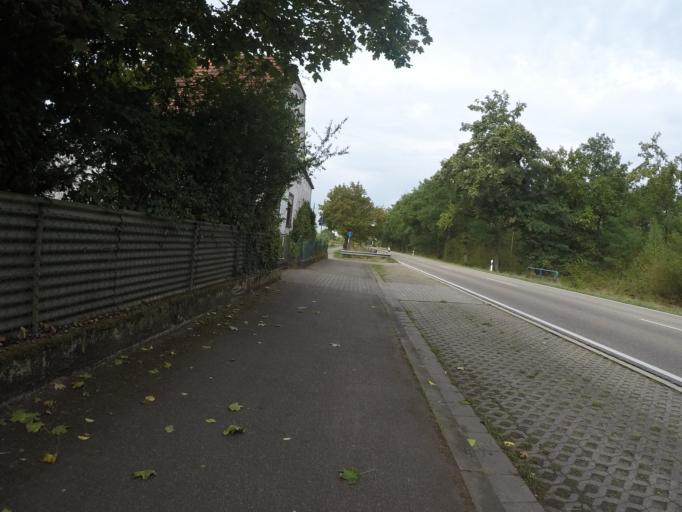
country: DE
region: Rheinland-Pfalz
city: Bohl-Iggelheim
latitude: 49.3567
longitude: 8.3292
